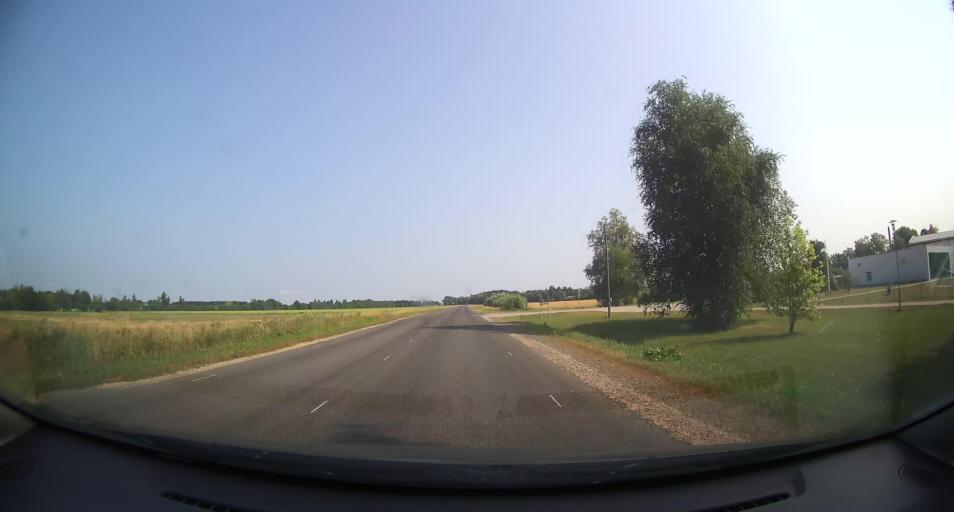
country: EE
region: Paernumaa
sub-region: Audru vald
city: Audru
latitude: 58.4747
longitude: 24.3270
